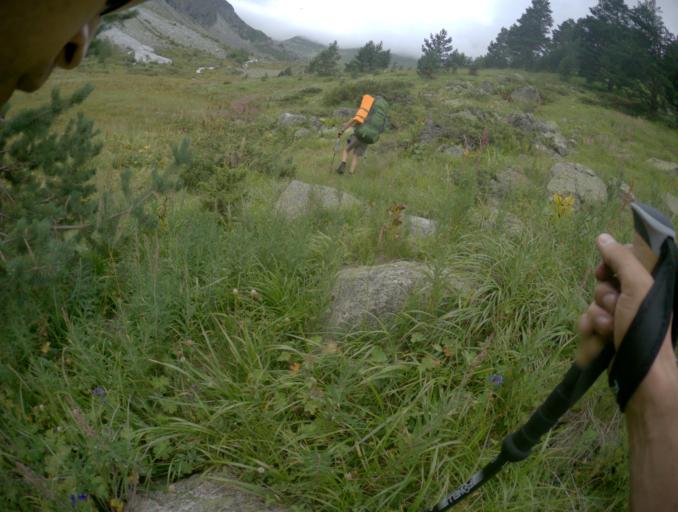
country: RU
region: Karachayevo-Cherkesiya
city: Uchkulan
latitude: 43.3361
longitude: 42.1266
